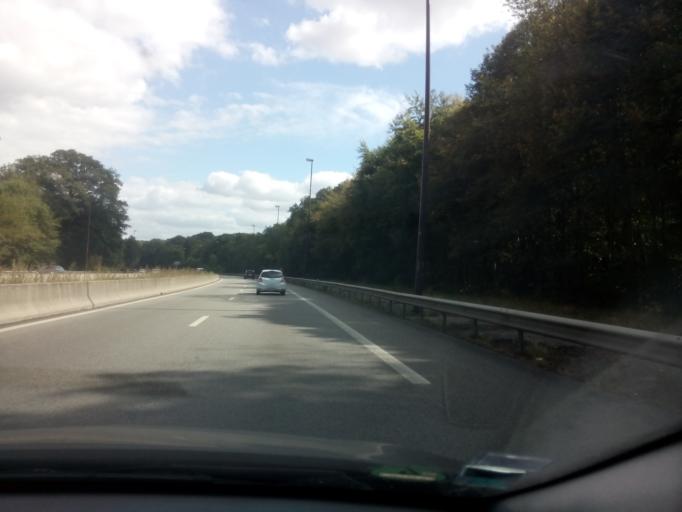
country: FR
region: Ile-de-France
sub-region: Departement des Hauts-de-Seine
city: Chatenay-Malabry
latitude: 48.7629
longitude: 2.2478
